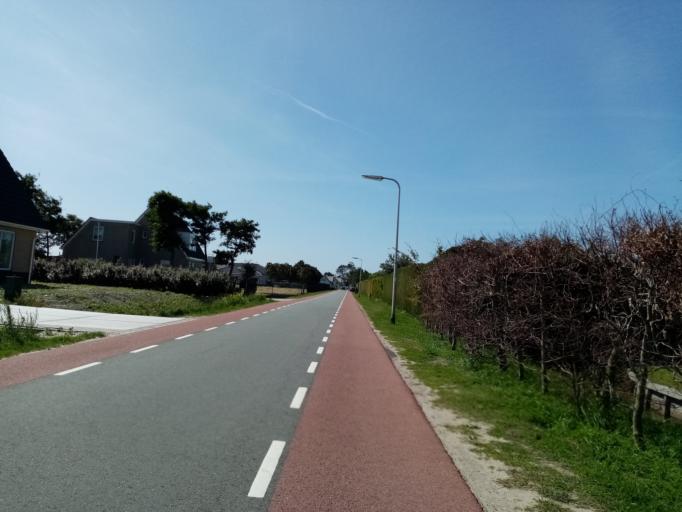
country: NL
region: South Holland
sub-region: Gemeente Noordwijkerhout
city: Noordwijkerhout
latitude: 52.2691
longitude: 4.4738
